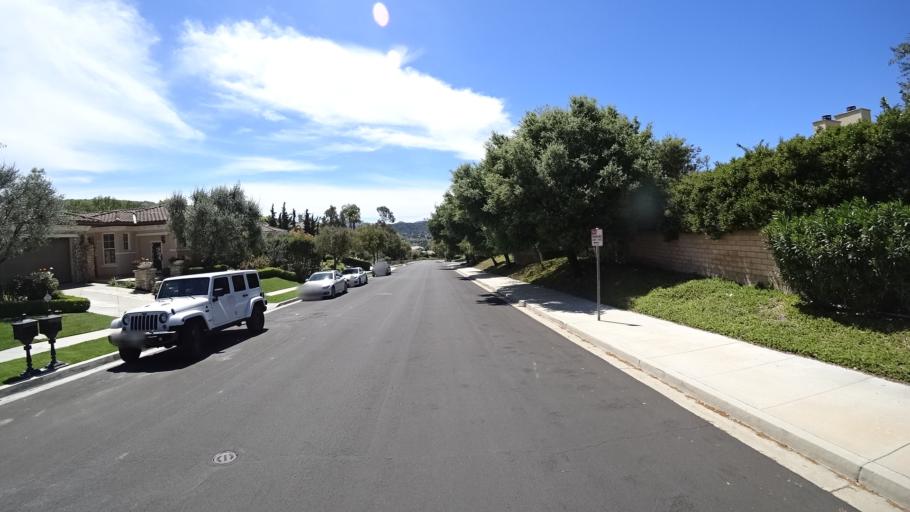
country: US
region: California
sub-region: Ventura County
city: Thousand Oaks
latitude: 34.1825
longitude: -118.8393
